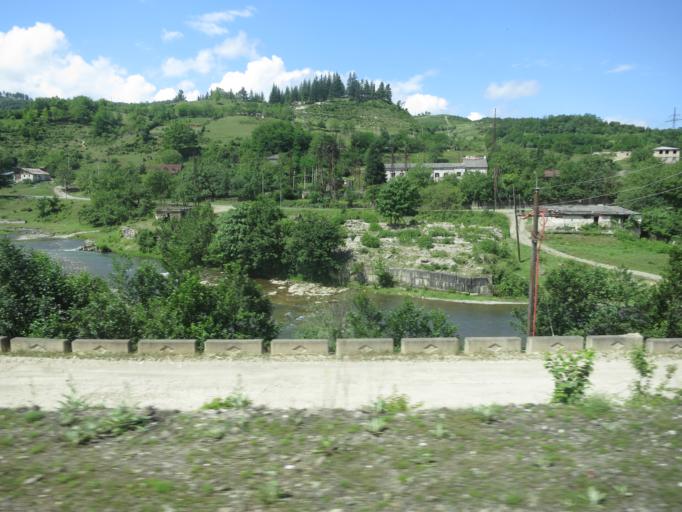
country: GE
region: Imereti
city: Kharagauli
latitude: 42.0268
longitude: 43.1982
